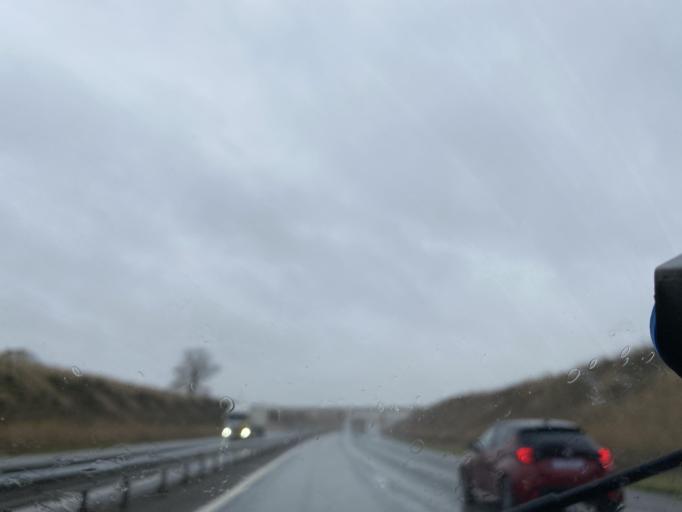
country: FR
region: Centre
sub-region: Departement d'Eure-et-Loir
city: Leves
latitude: 48.5343
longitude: 1.4544
